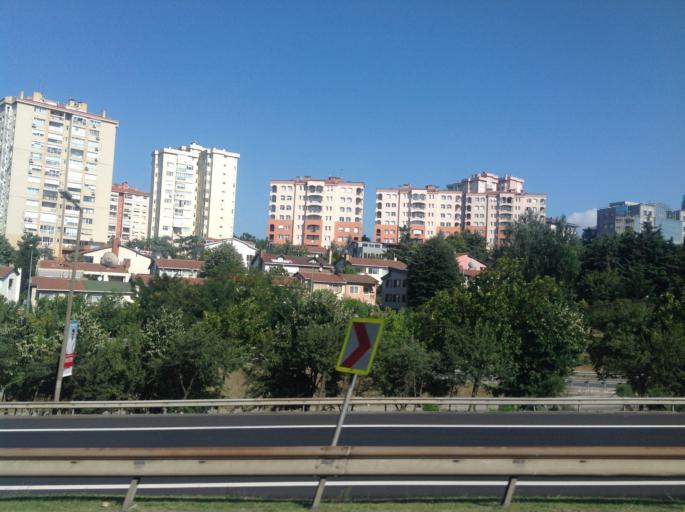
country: TR
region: Istanbul
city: Sisli
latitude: 41.0900
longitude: 29.0192
